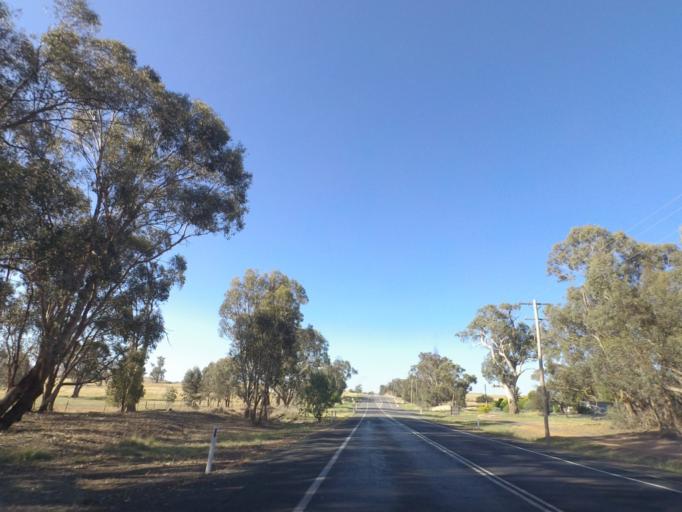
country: AU
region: New South Wales
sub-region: Wagga Wagga
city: Forest Hill
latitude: -35.2697
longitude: 147.7449
